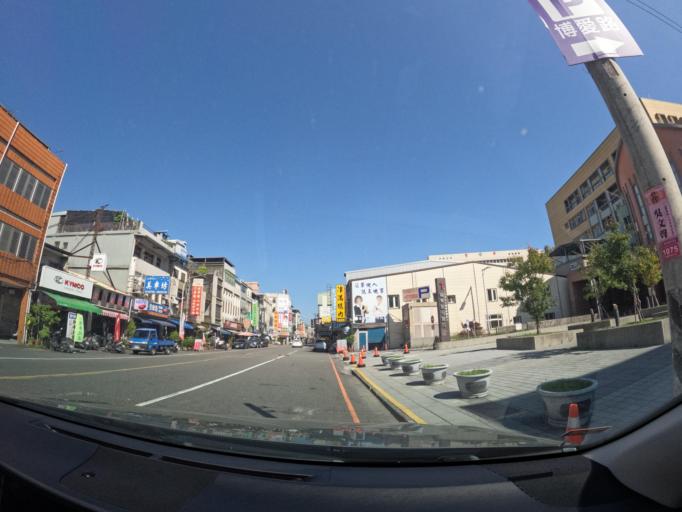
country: TW
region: Taiwan
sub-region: Yilan
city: Yilan
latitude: 24.6701
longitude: 121.7714
